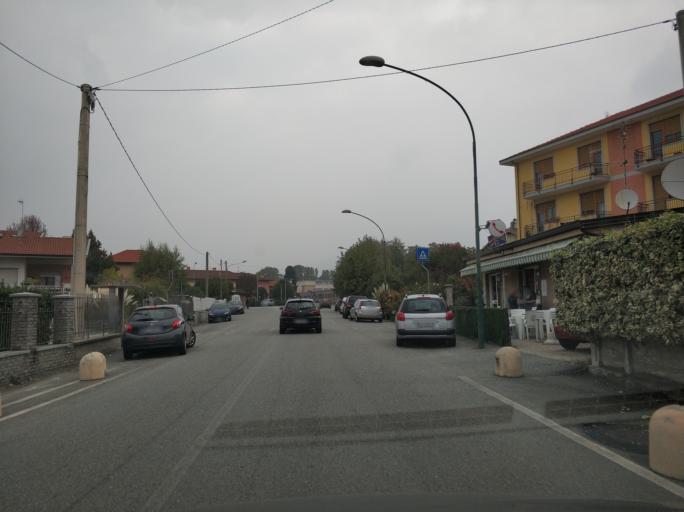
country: IT
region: Piedmont
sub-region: Provincia di Torino
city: Mathi
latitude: 45.2528
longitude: 7.5485
